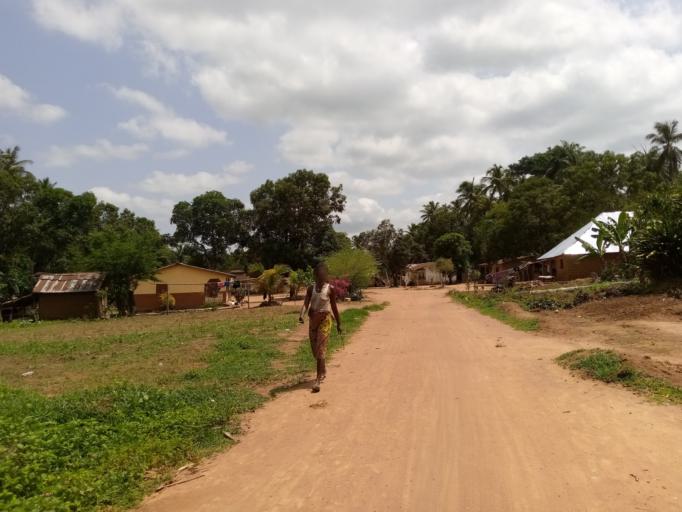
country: SL
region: Western Area
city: Waterloo
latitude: 8.3898
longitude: -12.9878
